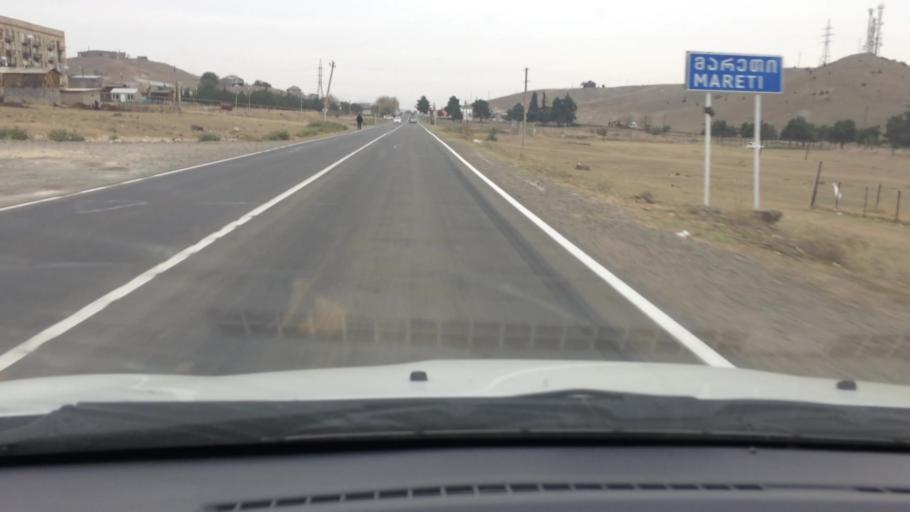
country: GE
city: Naghvarevi
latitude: 41.3596
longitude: 44.8336
